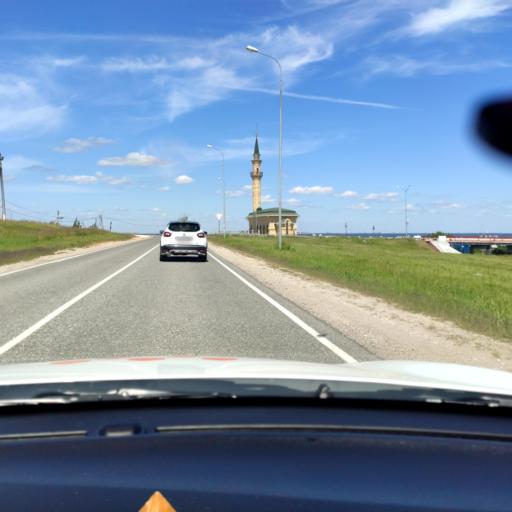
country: RU
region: Tatarstan
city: Osinovo
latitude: 55.7729
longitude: 48.8363
